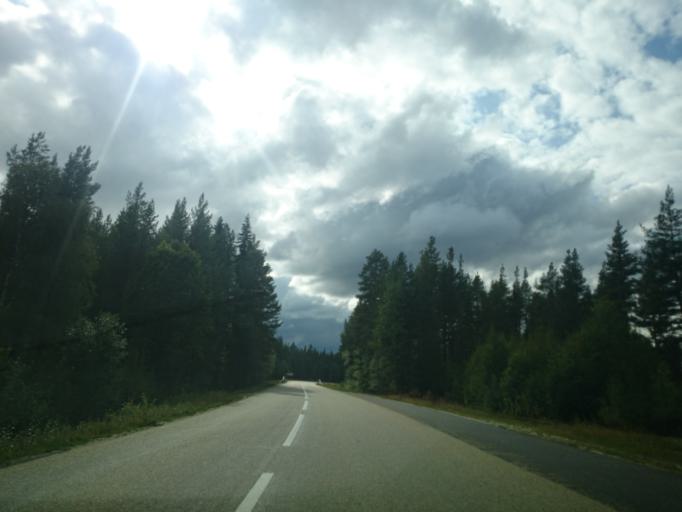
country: SE
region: Jaemtland
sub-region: Harjedalens Kommun
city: Sveg
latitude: 62.4134
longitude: 13.6169
